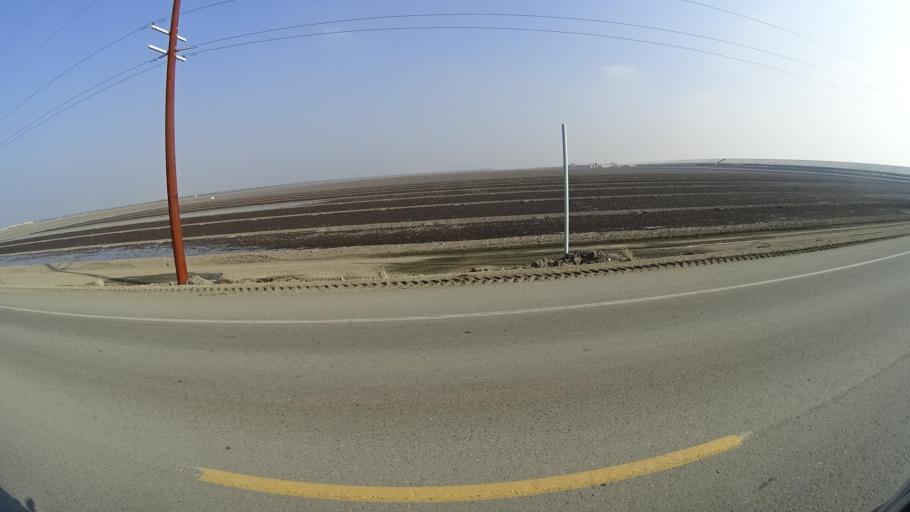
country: US
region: California
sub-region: Kern County
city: Greenfield
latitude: 35.1748
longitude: -119.1100
